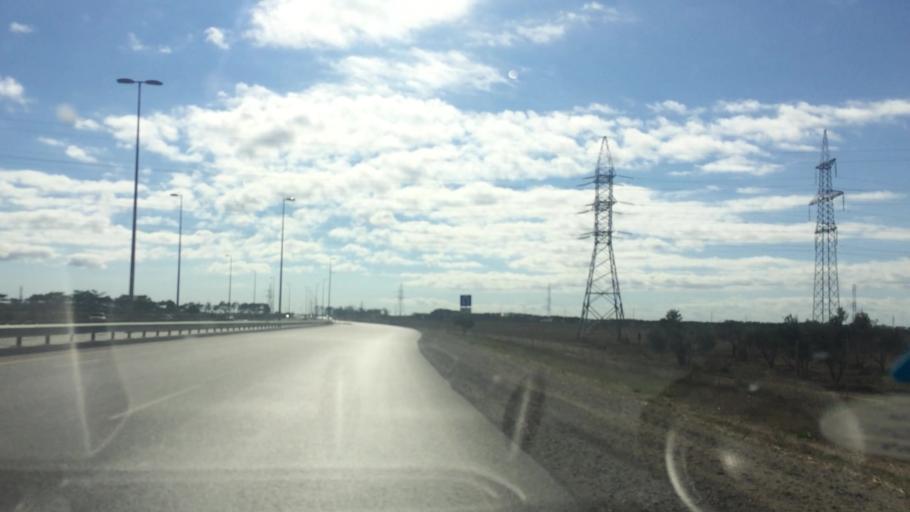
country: AZ
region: Baki
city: Qala
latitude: 40.4376
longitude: 50.1837
